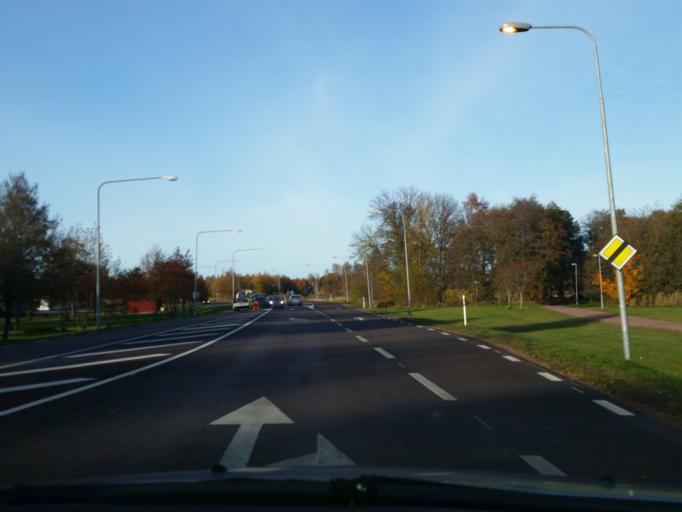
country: AX
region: Mariehamns stad
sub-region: Mariehamn
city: Mariehamn
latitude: 60.1108
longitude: 19.9432
